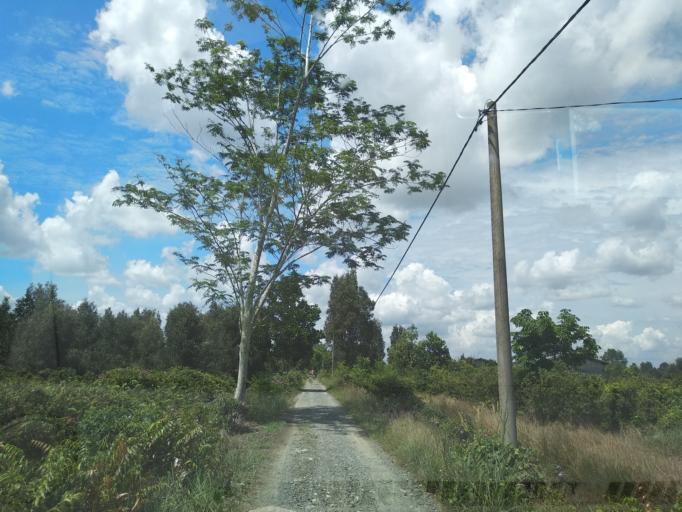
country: ID
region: South Kalimantan
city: Sungaipuntik
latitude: -3.1791
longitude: 114.7348
